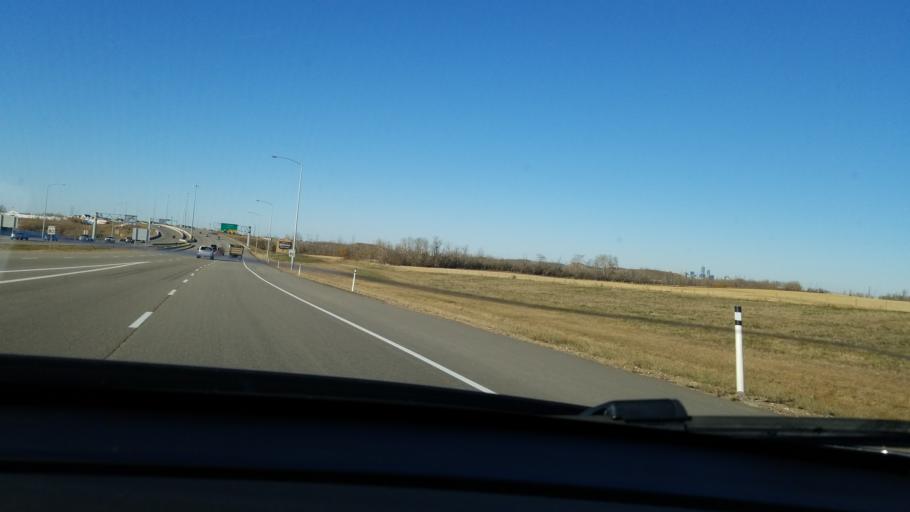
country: CA
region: Alberta
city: Sherwood Park
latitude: 53.4831
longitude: -113.3516
